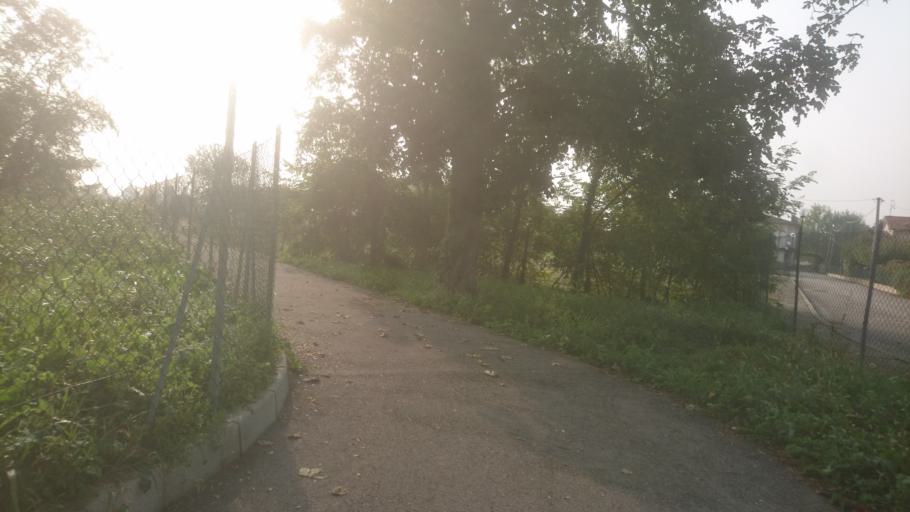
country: IT
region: Veneto
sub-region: Provincia di Vicenza
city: Grisignano di Zocco
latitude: 45.4859
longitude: 11.7268
